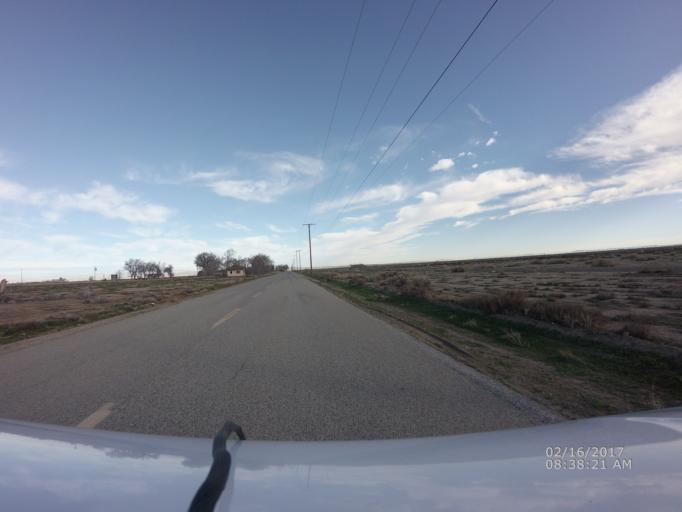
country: US
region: California
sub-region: Los Angeles County
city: Lancaster
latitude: 34.7543
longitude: -118.0054
